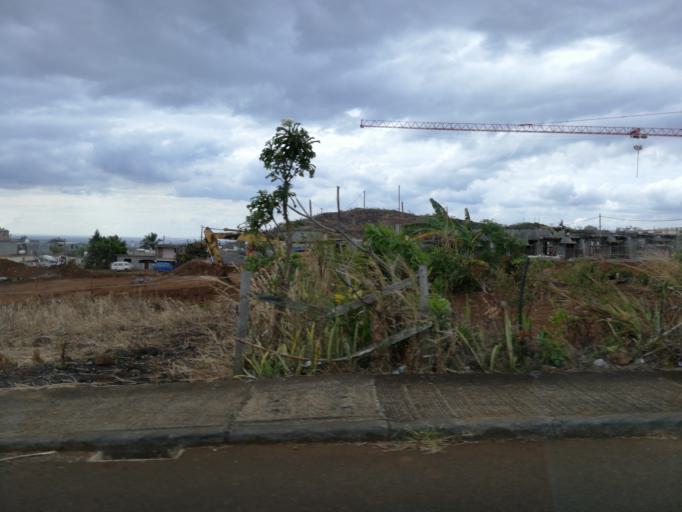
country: MU
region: Black River
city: Petite Riviere
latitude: -20.2130
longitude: 57.4634
